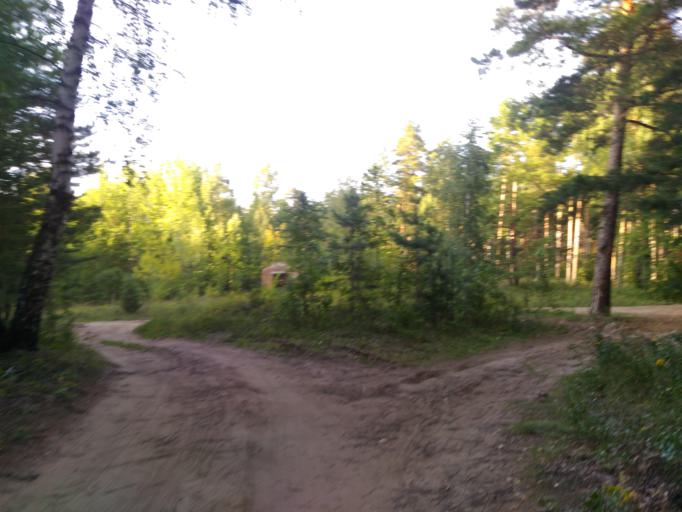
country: RU
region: Ulyanovsk
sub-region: Ulyanovskiy Rayon
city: Ulyanovsk
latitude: 54.3564
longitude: 48.5173
